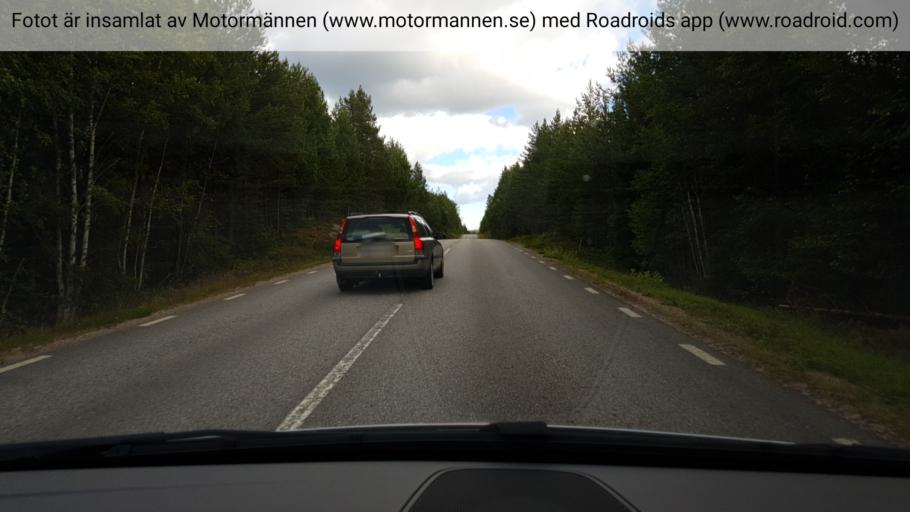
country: SE
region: Jaemtland
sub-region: Harjedalens Kommun
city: Sveg
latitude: 62.0282
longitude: 14.7937
